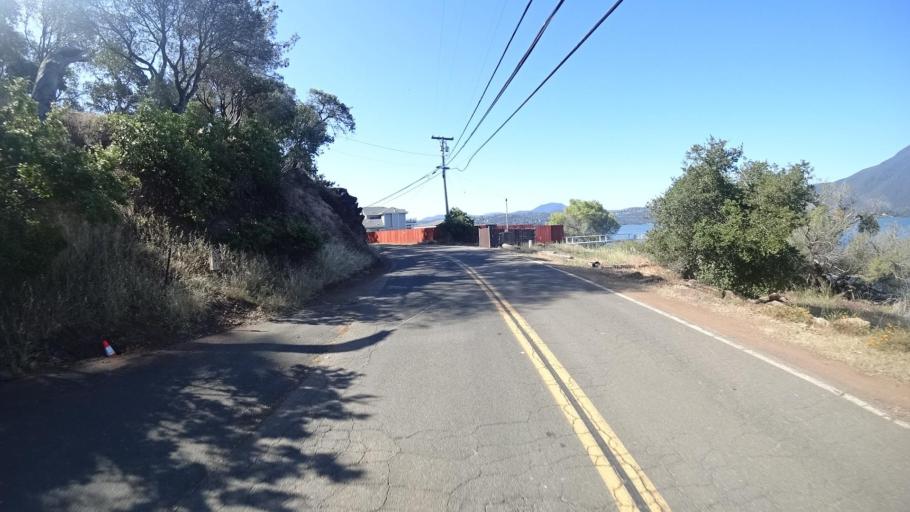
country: US
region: California
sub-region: Lake County
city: Clearlake Oaks
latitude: 38.9947
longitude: -122.7052
